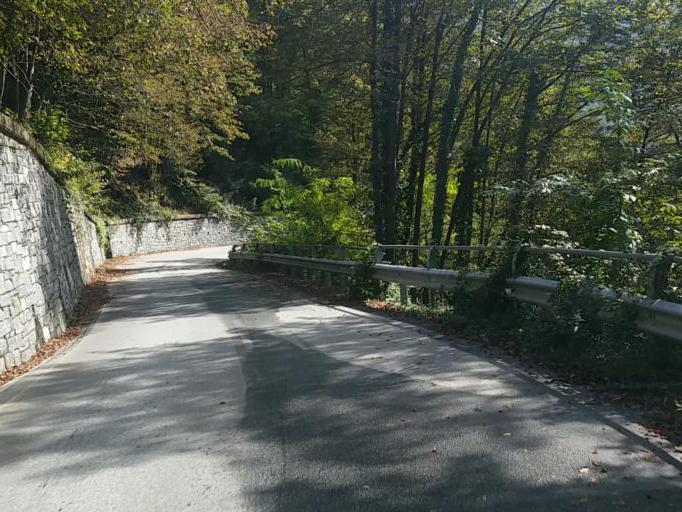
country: IT
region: Piedmont
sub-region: Provincia Verbano-Cusio-Ossola
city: Falmenta
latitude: 46.0934
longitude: 8.5893
